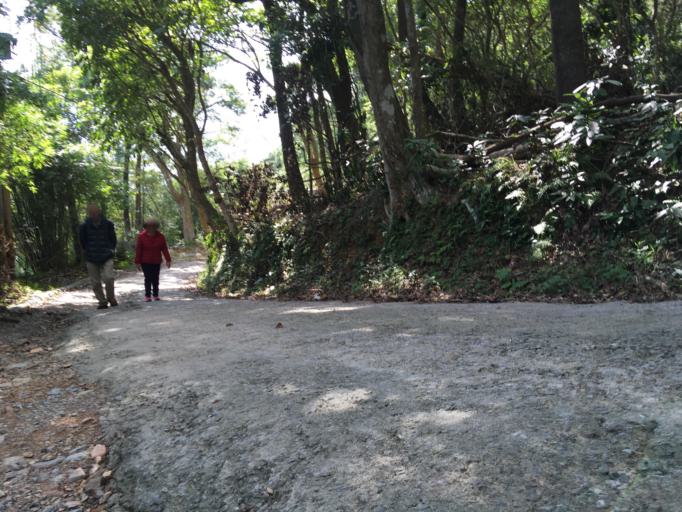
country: TW
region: Taiwan
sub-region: Yilan
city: Yilan
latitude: 24.8415
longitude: 121.7763
